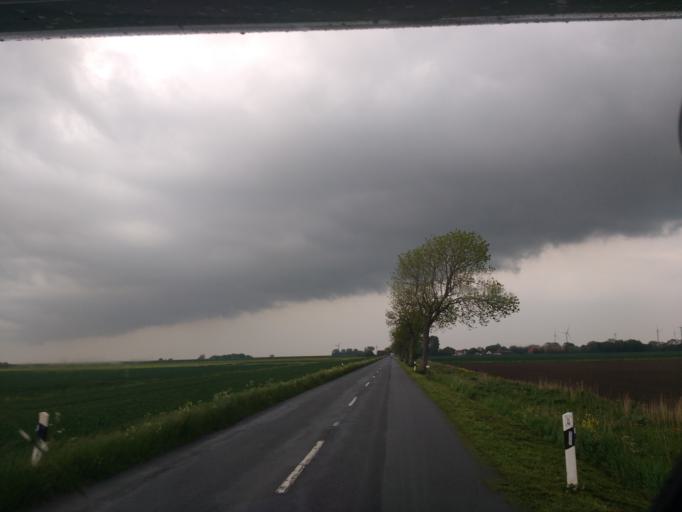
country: DE
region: Lower Saxony
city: Wangerooge
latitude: 53.6969
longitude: 7.8842
